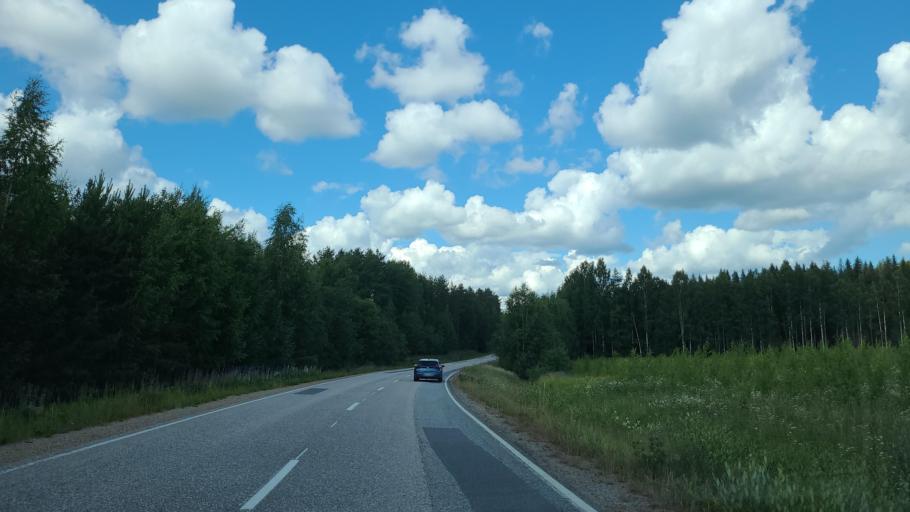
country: FI
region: Northern Savo
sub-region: Koillis-Savo
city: Kaavi
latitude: 62.9105
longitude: 28.7102
